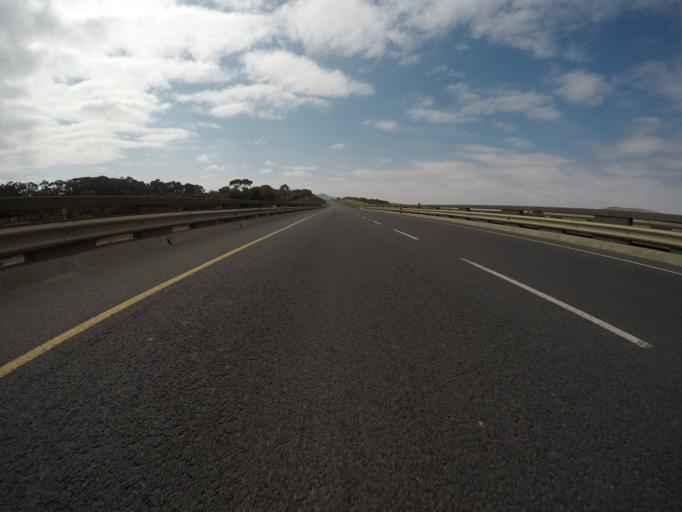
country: ZA
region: Western Cape
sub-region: City of Cape Town
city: Sunset Beach
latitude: -33.7897
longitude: 18.5485
